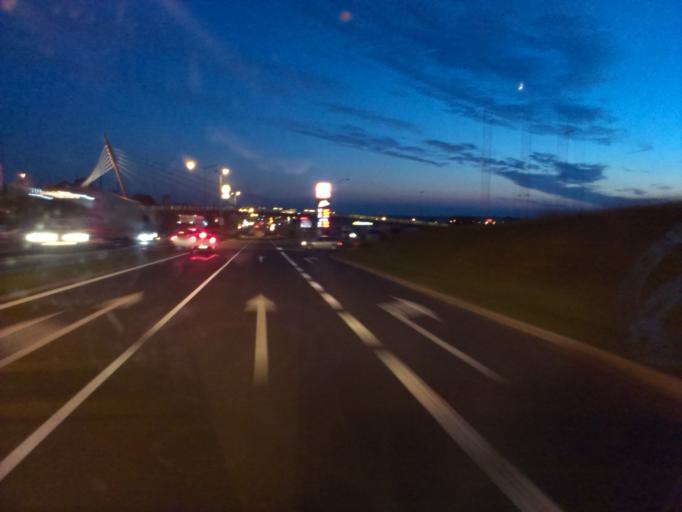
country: PL
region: Lower Silesian Voivodeship
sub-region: Powiat polkowicki
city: Polkowice
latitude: 51.5076
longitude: 16.0635
